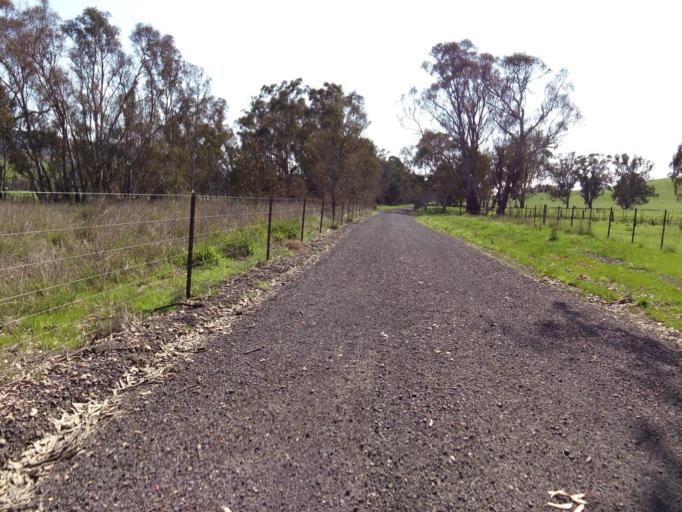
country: AU
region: Victoria
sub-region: Murrindindi
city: Alexandra
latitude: -37.1433
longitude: 145.5889
